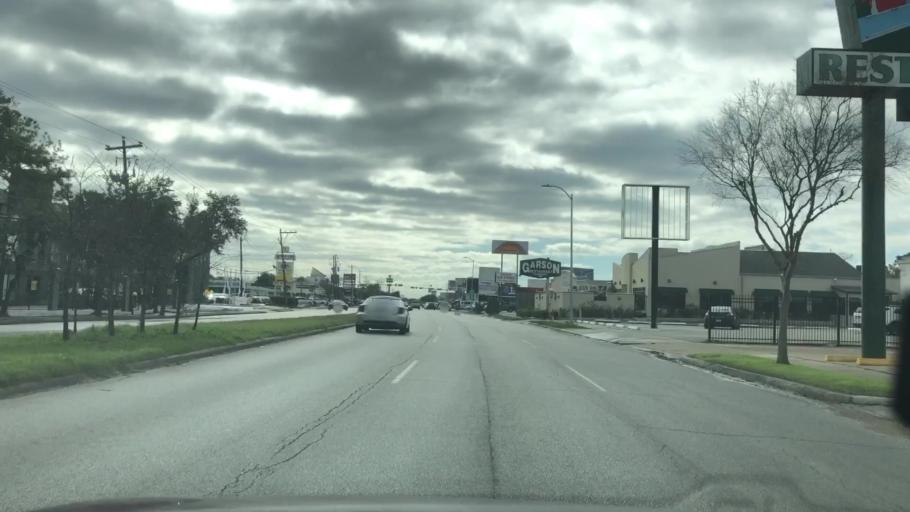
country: US
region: Texas
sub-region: Harris County
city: Piney Point Village
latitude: 29.7340
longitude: -95.5013
